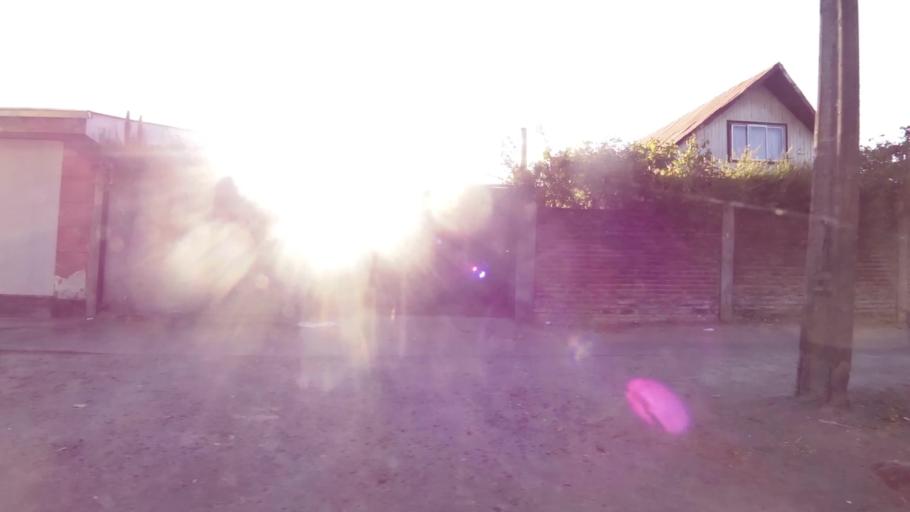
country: CL
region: Maule
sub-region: Provincia de Talca
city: Talca
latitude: -35.4349
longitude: -71.6471
